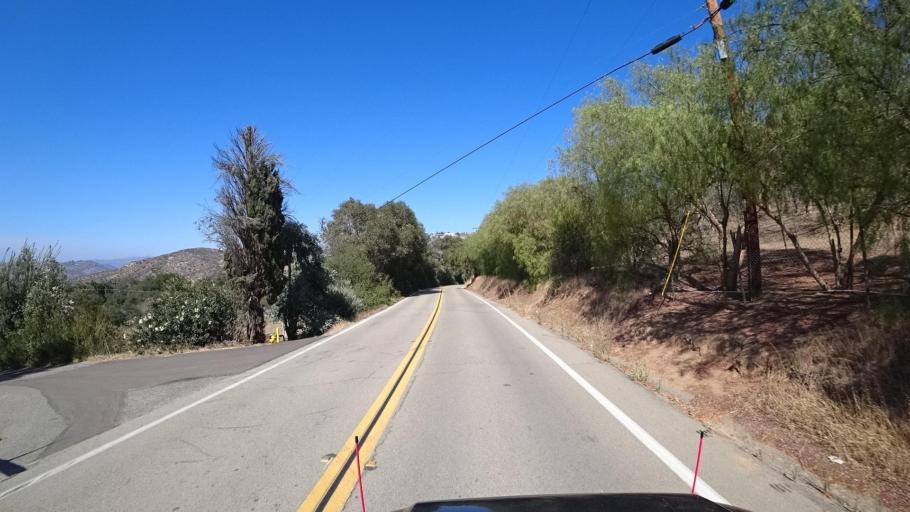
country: US
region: California
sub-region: San Diego County
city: Bonsall
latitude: 33.2971
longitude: -117.1679
